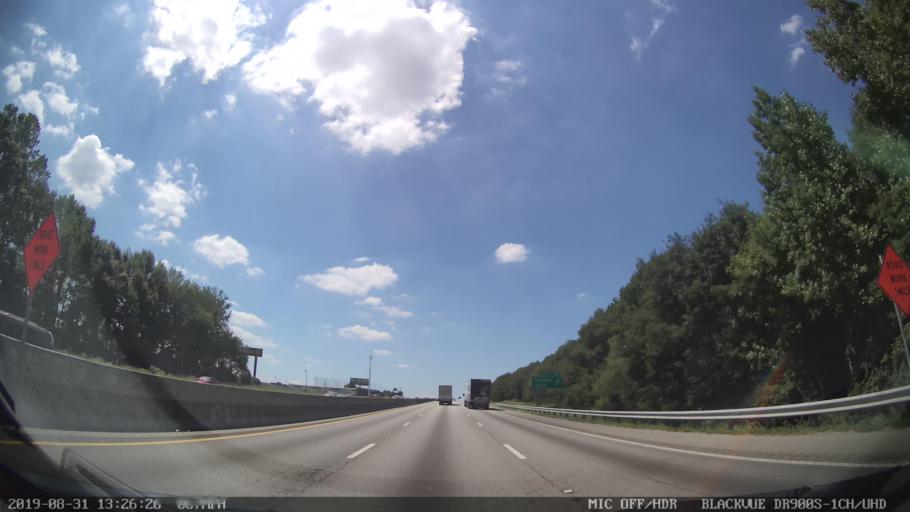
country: US
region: South Carolina
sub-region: Greenville County
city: Five Forks
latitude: 34.8608
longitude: -82.2522
